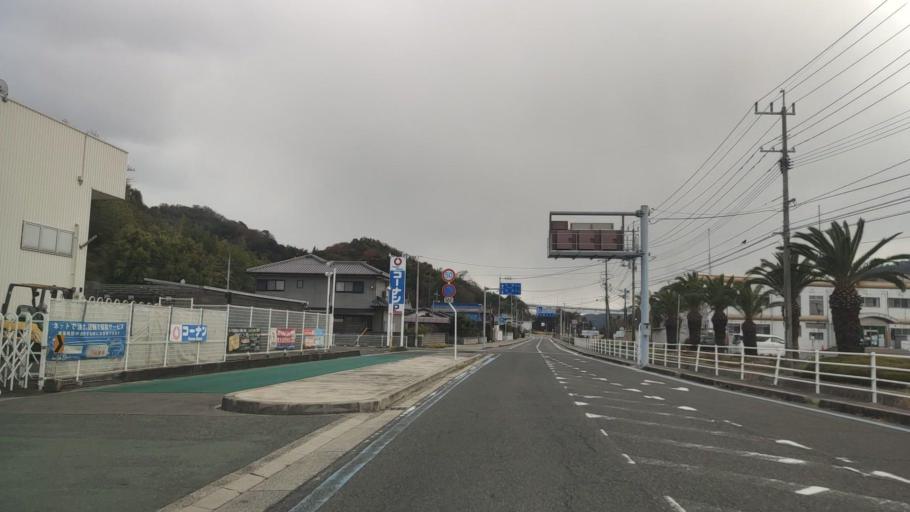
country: JP
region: Hiroshima
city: Innoshima
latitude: 34.2039
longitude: 133.0757
